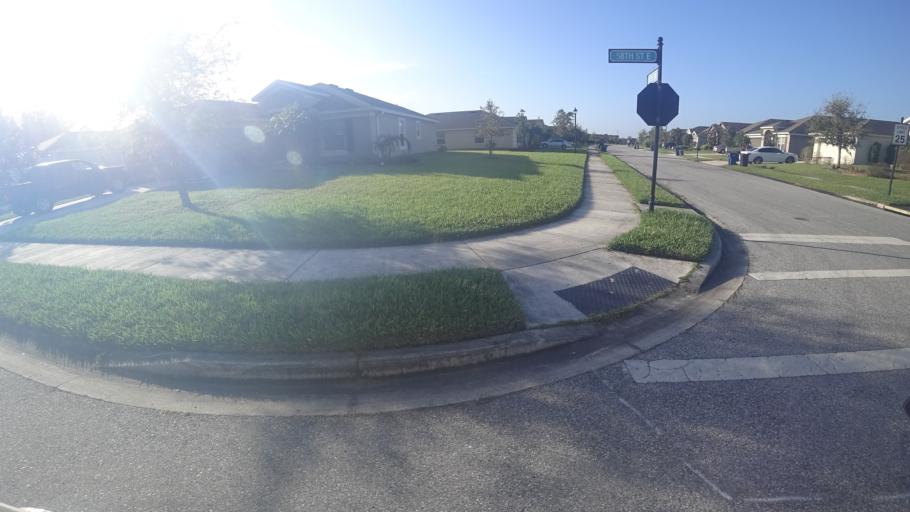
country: US
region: Florida
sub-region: Manatee County
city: Ellenton
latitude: 27.5687
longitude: -82.4539
